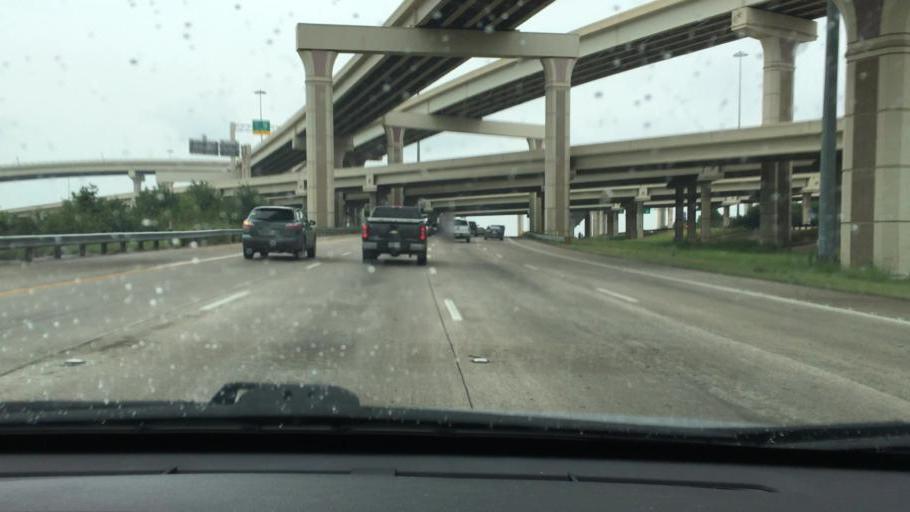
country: US
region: Texas
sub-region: Bexar County
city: Balcones Heights
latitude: 29.4996
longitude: -98.5497
